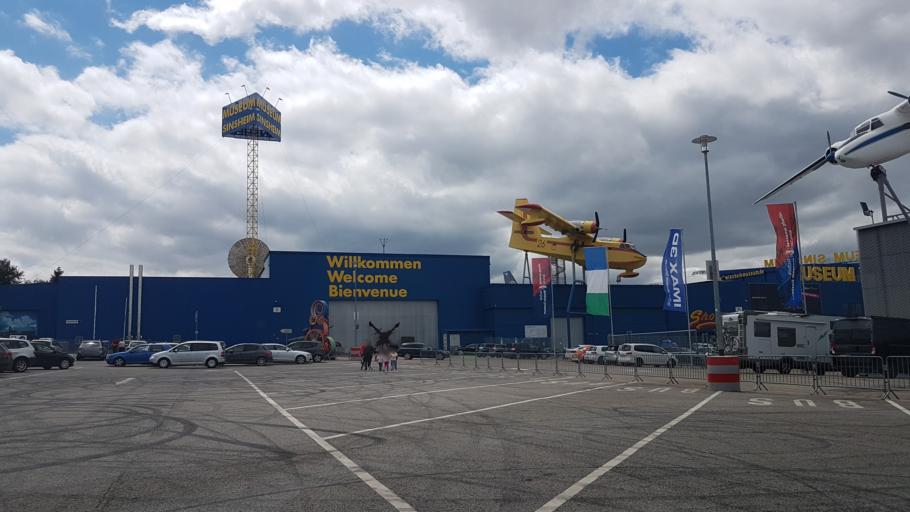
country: DE
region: Baden-Wuerttemberg
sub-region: Karlsruhe Region
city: Sinsheim
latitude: 49.2387
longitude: 8.8990
